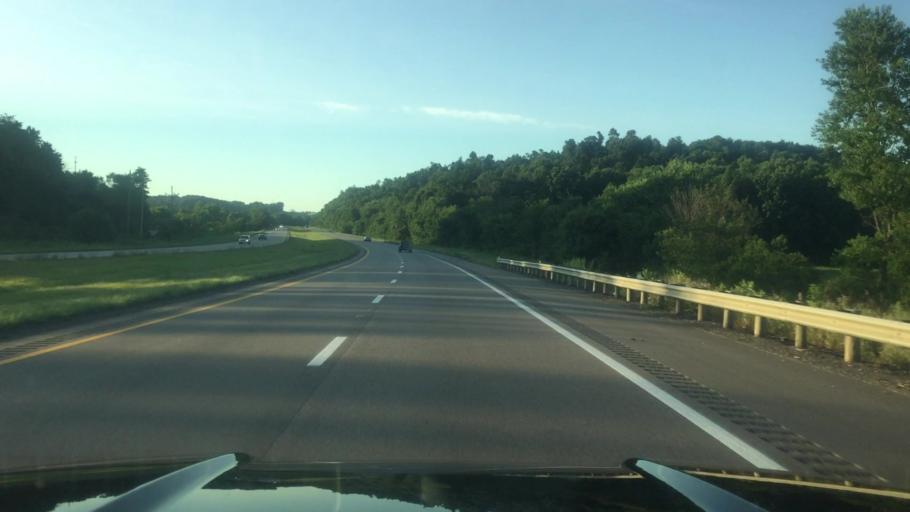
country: US
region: Ohio
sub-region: Tuscarawas County
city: Newcomerstown
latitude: 40.3236
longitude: -81.5691
